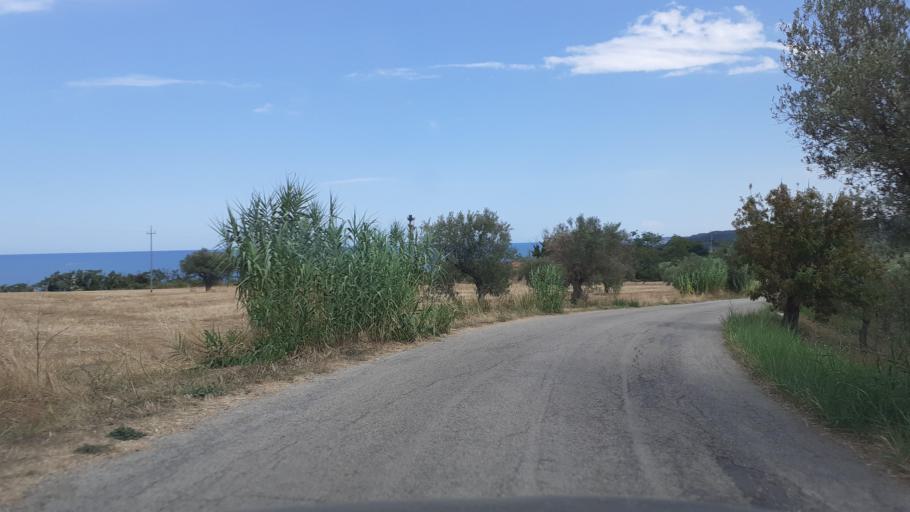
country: IT
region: Abruzzo
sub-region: Provincia di Chieti
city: Fossacesia
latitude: 42.2514
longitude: 14.5026
